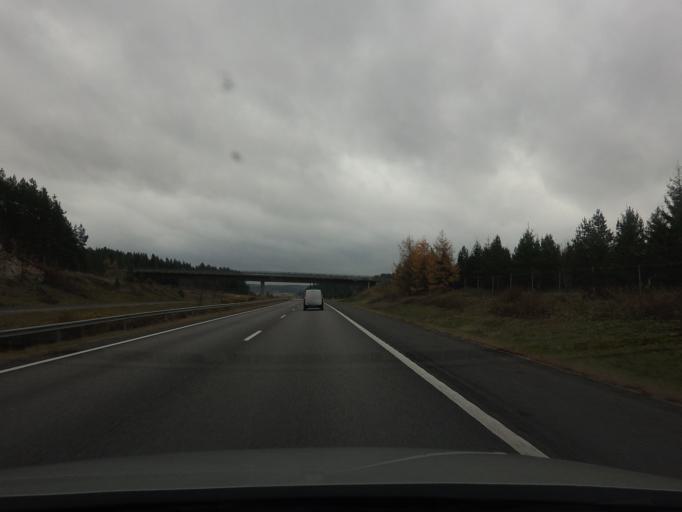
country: FI
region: Varsinais-Suomi
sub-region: Turku
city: Paimio
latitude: 60.4370
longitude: 22.6337
